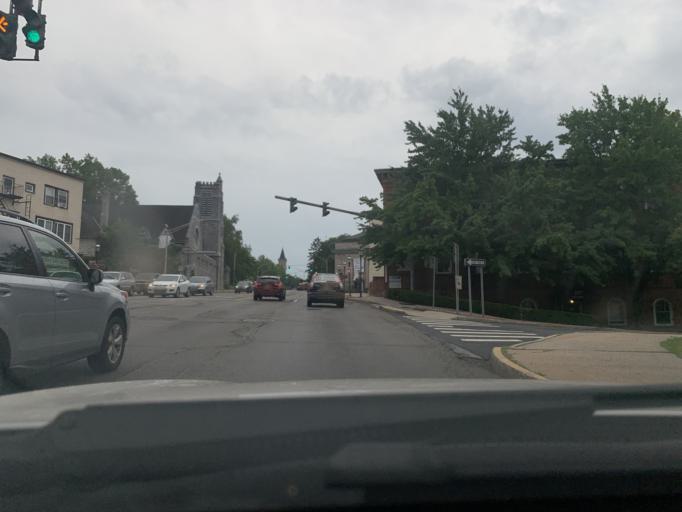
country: US
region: New York
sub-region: Westchester County
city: Ossining
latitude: 41.1629
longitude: -73.8617
